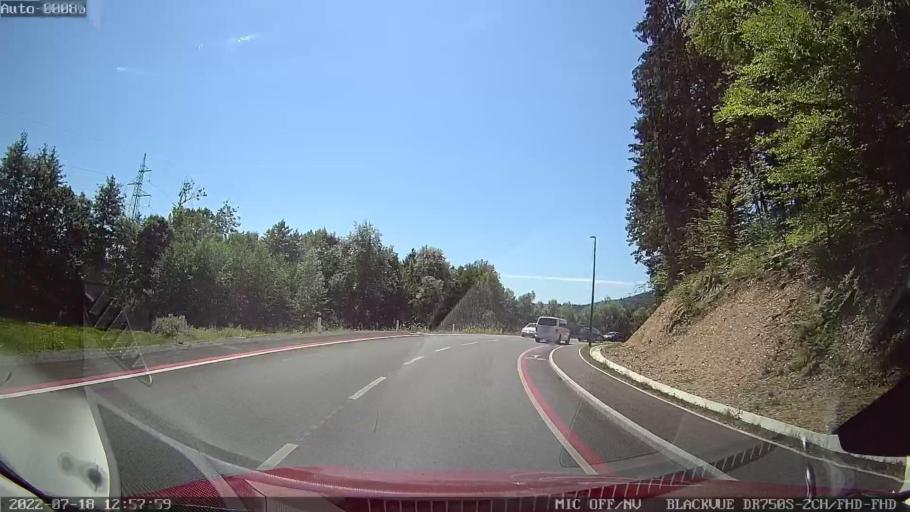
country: SI
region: Dobrova-Horjul-Polhov Gradec
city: Dobrova
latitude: 46.0651
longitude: 14.4199
